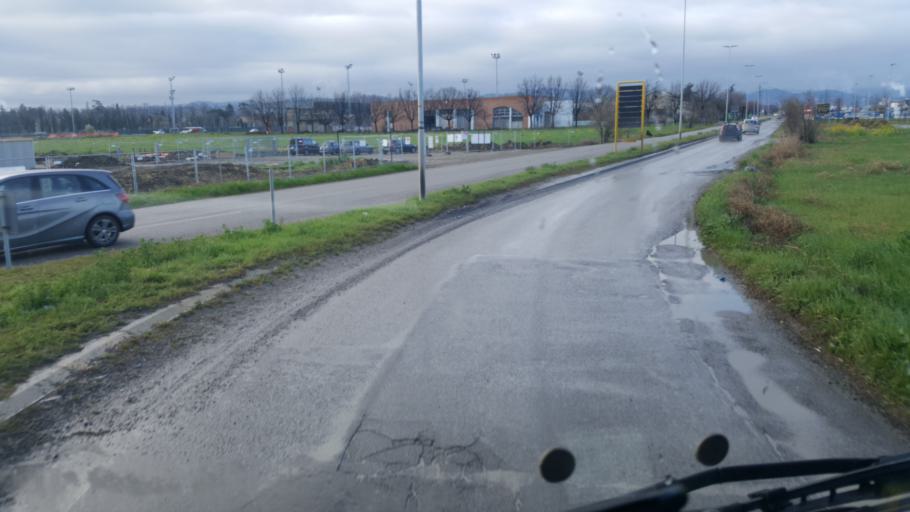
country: IT
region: Emilia-Romagna
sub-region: Provincia di Modena
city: Sassuolo
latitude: 44.5647
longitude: 10.7918
